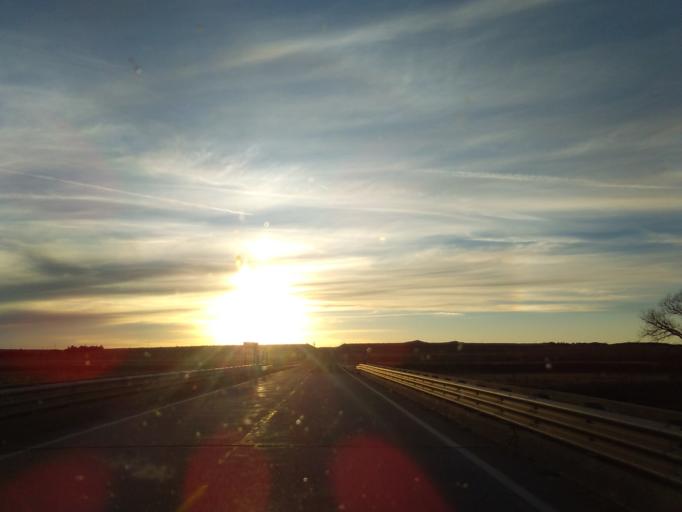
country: US
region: Kansas
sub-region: Wallace County
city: Sharon Springs
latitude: 39.0177
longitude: -101.3483
